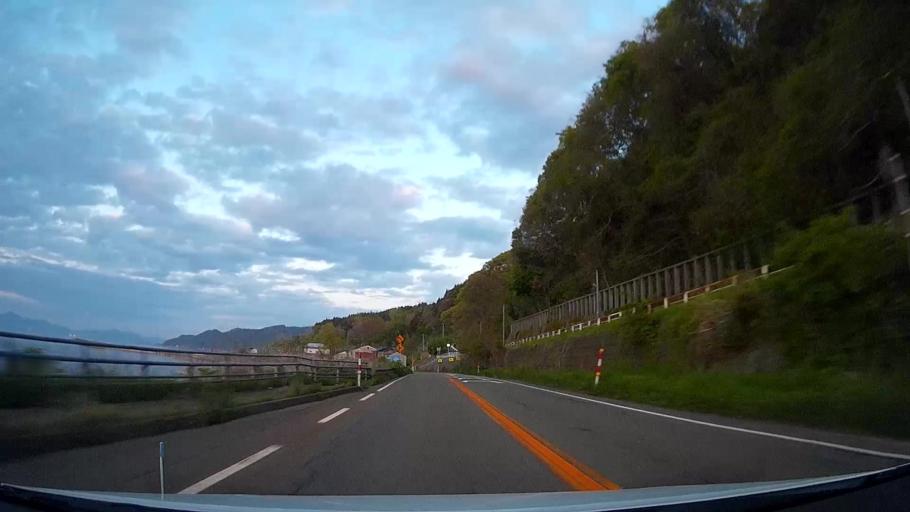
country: JP
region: Niigata
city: Joetsu
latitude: 37.1640
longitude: 138.1317
